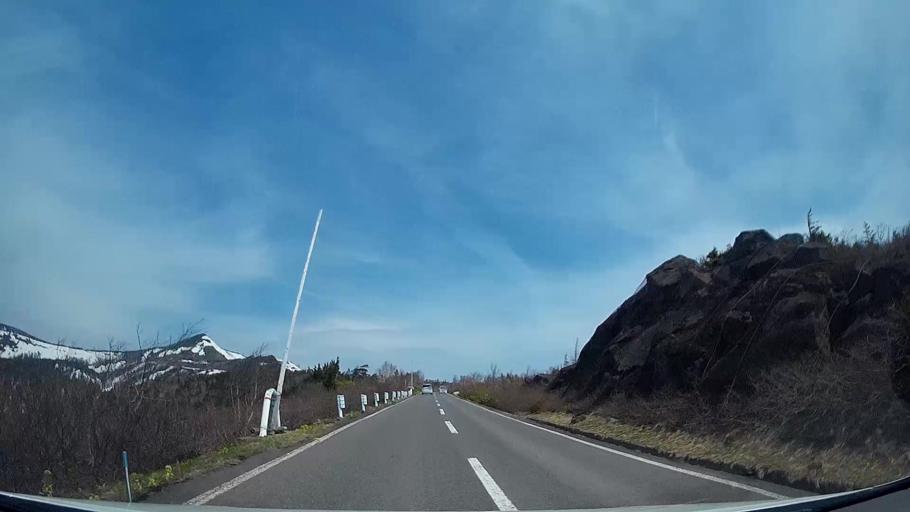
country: JP
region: Iwate
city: Shizukuishi
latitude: 39.9353
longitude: 140.9110
